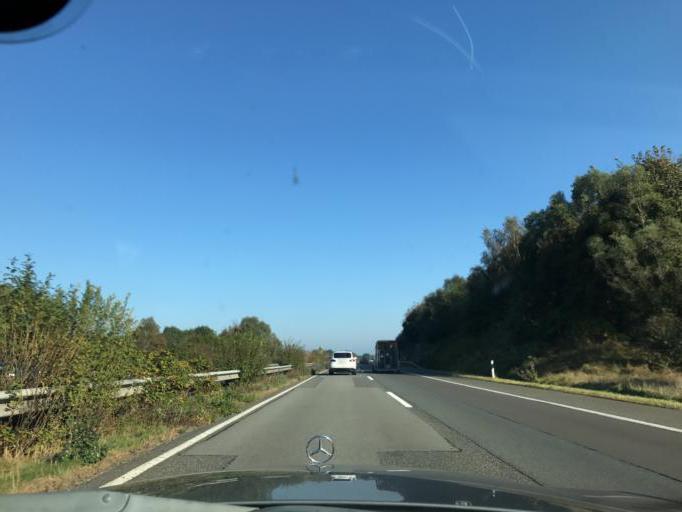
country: DE
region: Lower Saxony
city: Leer
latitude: 53.2630
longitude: 7.4564
